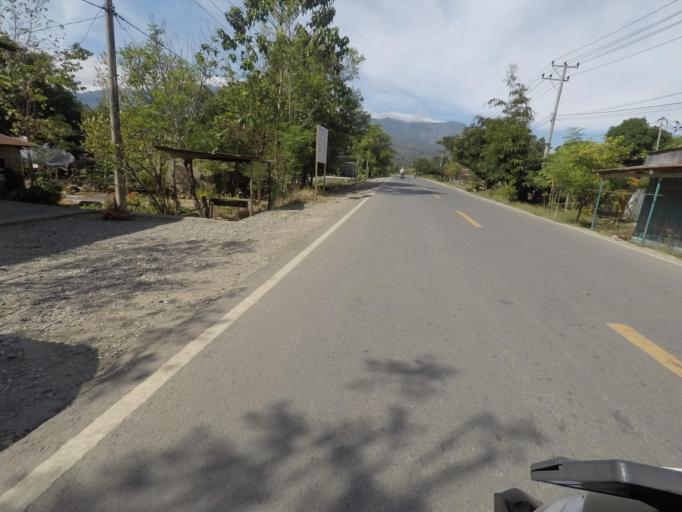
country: TL
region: Bobonaro
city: Maliana
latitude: -8.9813
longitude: 125.2210
